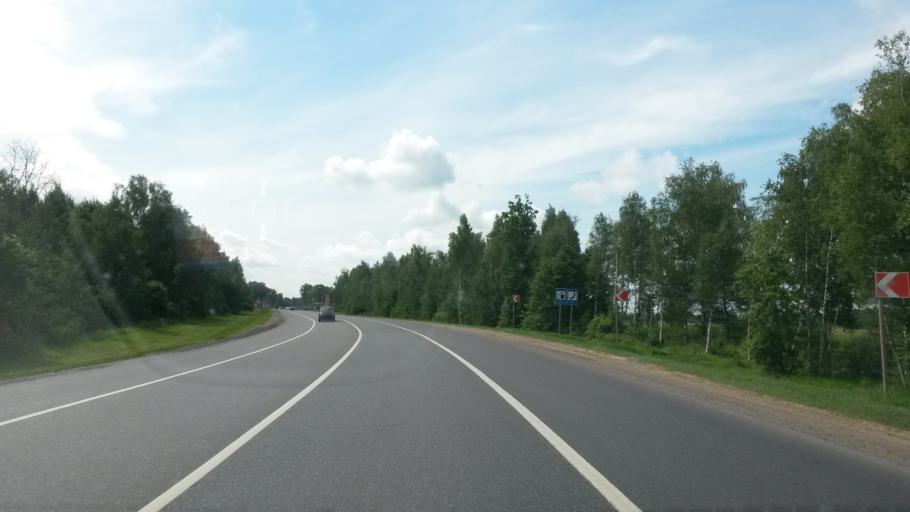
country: RU
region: Jaroslavl
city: Porech'ye-Rybnoye
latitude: 57.1100
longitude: 39.3170
